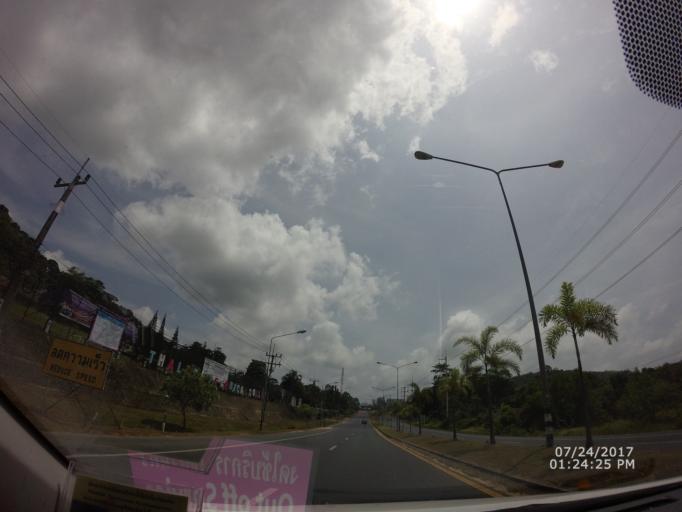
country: TH
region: Phuket
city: Thalang
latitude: 8.0899
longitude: 98.3241
